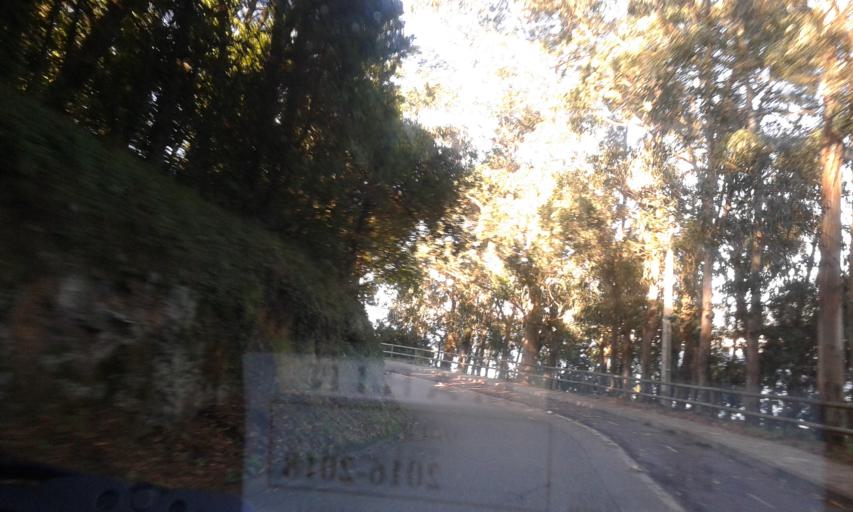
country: ES
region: Galicia
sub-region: Provincia de Pontevedra
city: Marin
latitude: 42.3848
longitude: -8.7245
